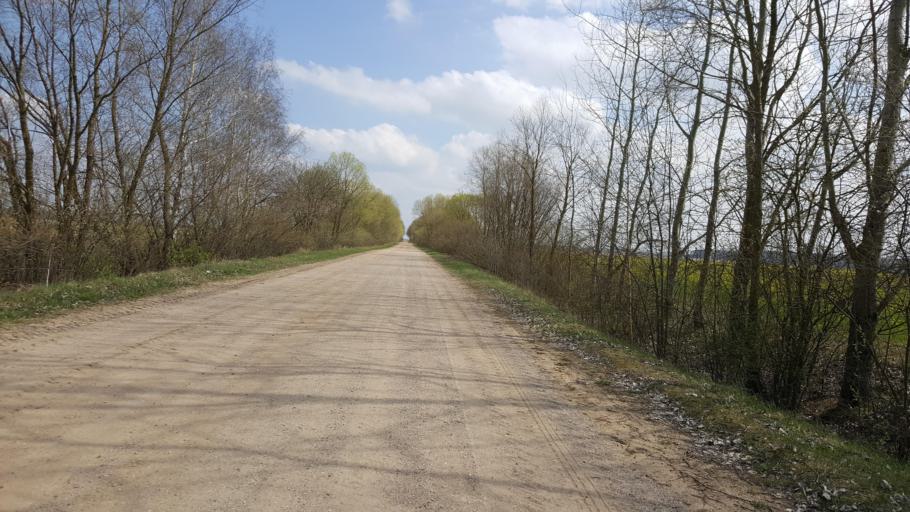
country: BY
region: Brest
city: Zhabinka
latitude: 52.2670
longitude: 24.0062
